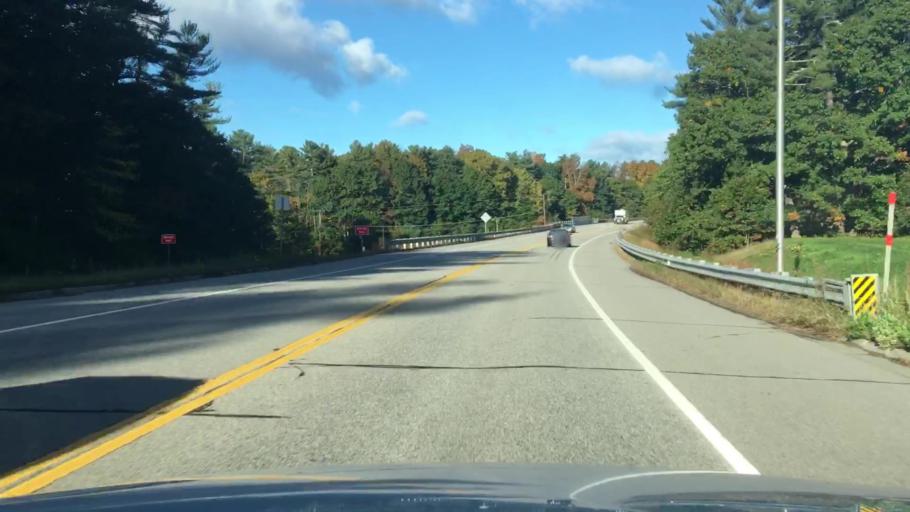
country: US
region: New Hampshire
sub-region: Strafford County
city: Durham
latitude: 43.1379
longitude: -70.9091
